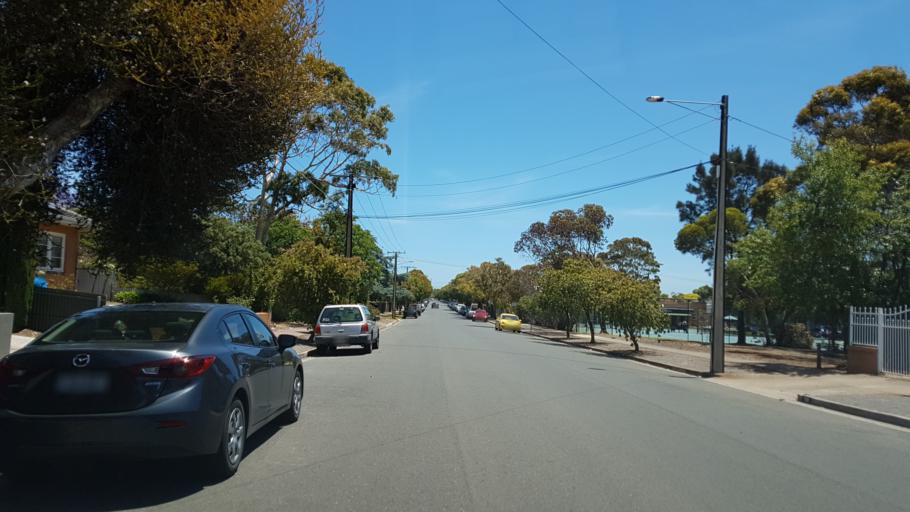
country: AU
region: South Australia
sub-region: Holdfast Bay
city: Seacliff Park
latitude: -35.0259
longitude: 138.5296
